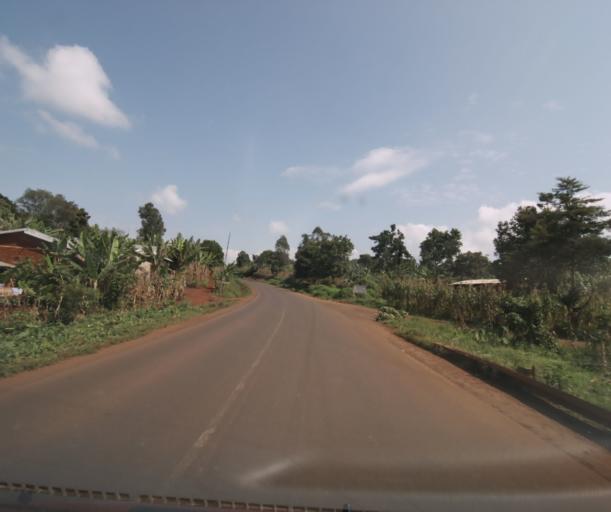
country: CM
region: West
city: Bansoa
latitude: 5.4919
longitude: 10.2637
